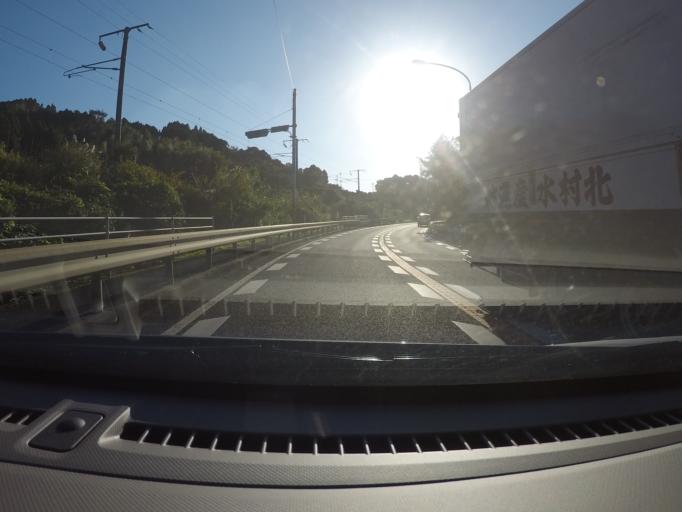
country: JP
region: Kagoshima
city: Izumi
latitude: 32.1500
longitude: 130.3634
